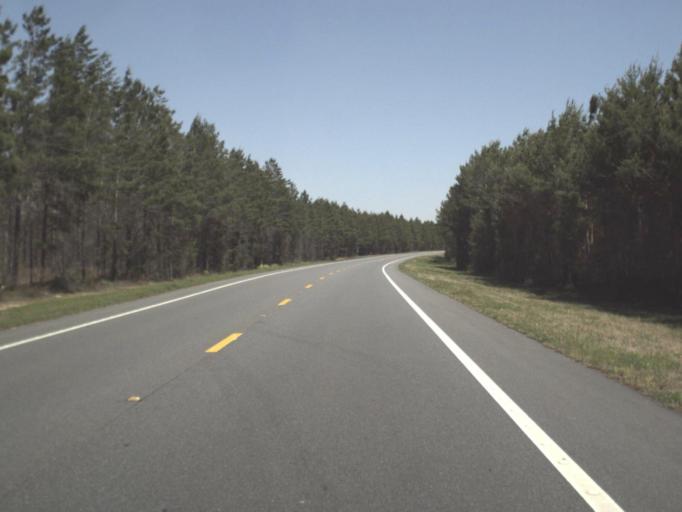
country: US
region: Florida
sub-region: Bay County
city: Youngstown
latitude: 30.4316
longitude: -85.2844
